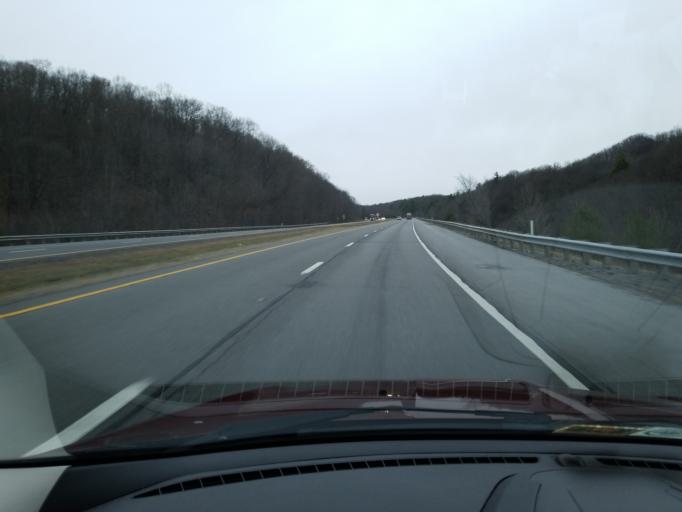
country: US
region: West Virginia
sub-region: Mercer County
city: Athens
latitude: 37.3439
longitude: -81.0135
